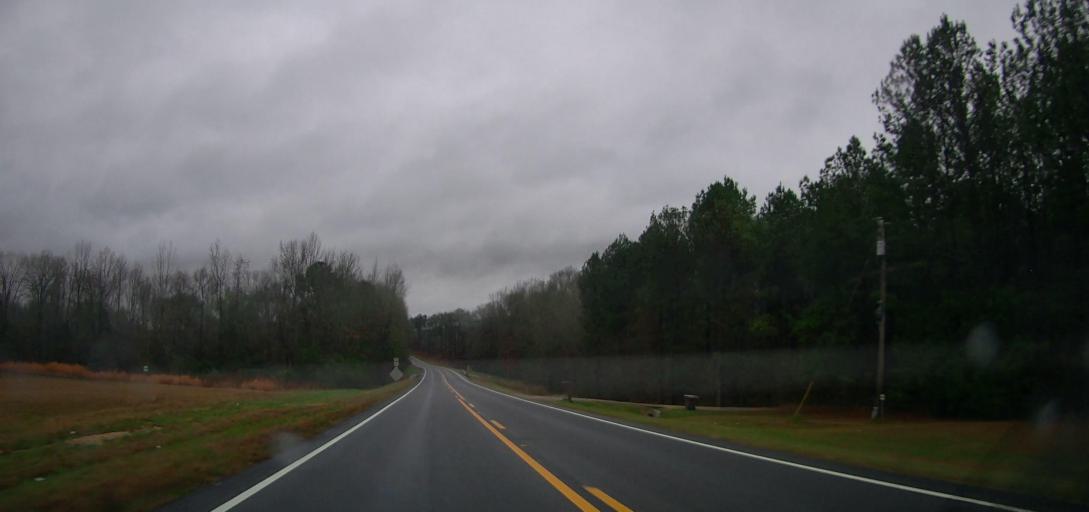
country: US
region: Alabama
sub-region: Bibb County
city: Centreville
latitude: 32.8360
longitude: -86.9550
